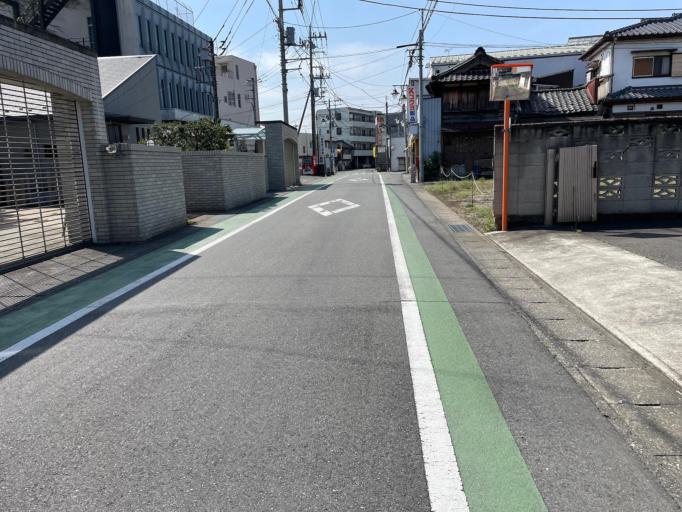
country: JP
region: Gunma
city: Takasaki
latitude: 36.2975
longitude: 139.0493
